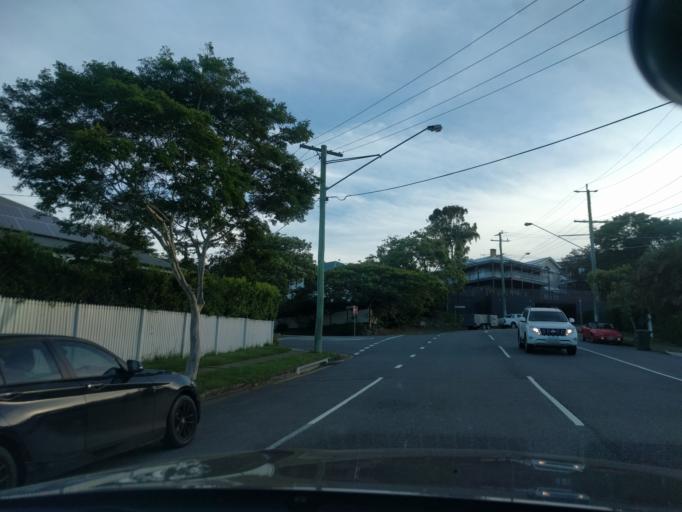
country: AU
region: Queensland
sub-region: Brisbane
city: Milton
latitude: -27.4714
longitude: 152.9955
